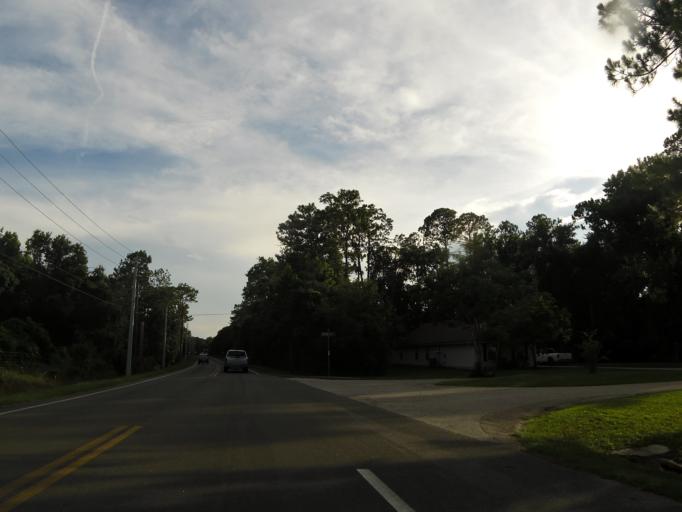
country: US
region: Florida
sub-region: Clay County
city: Green Cove Springs
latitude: 30.0120
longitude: -81.6104
